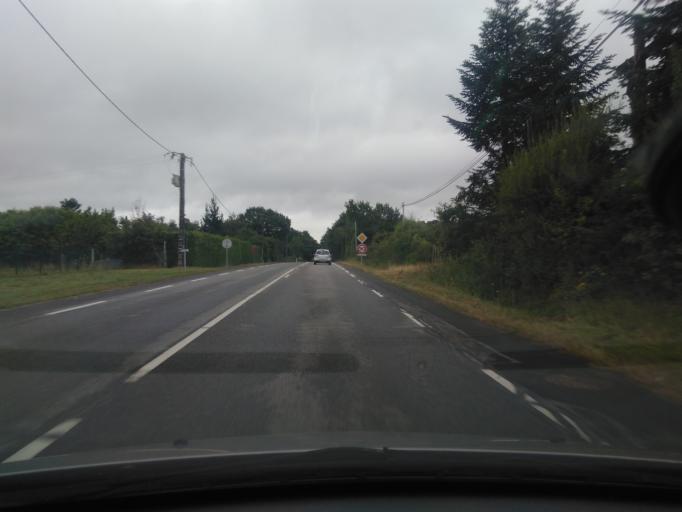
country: FR
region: Pays de la Loire
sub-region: Departement de la Vendee
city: Nesmy
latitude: 46.6186
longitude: -1.3608
